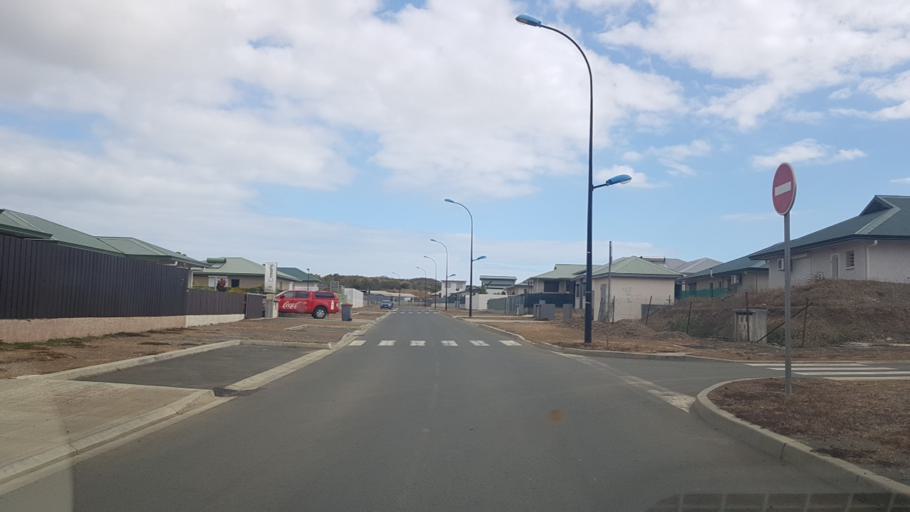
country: NC
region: South Province
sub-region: Dumbea
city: Dumbea
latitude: -22.2003
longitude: 166.4417
